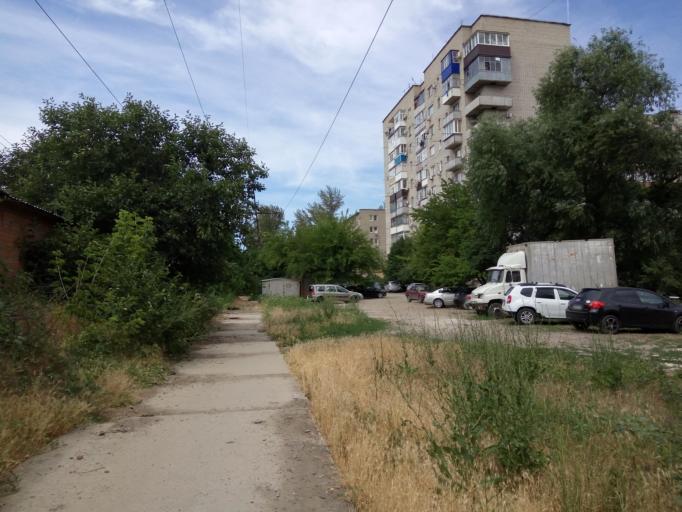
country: RU
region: Rostov
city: Bataysk
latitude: 47.1216
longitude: 39.7327
